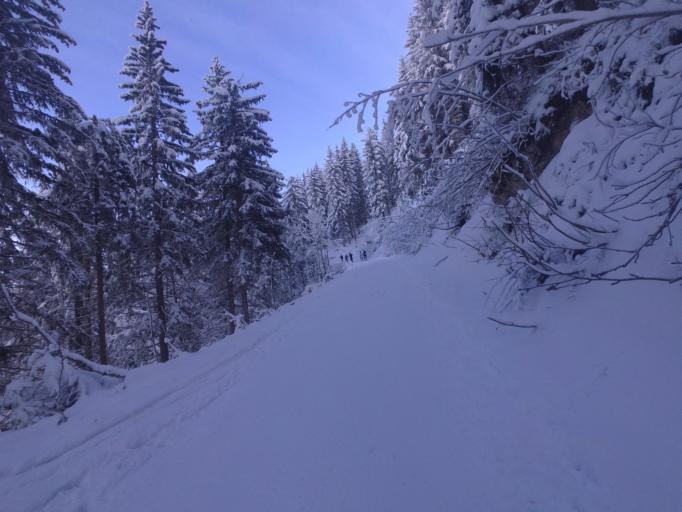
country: AT
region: Salzburg
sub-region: Politischer Bezirk Sankt Johann im Pongau
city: Sankt Johann im Pongau
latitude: 47.3155
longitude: 13.2245
